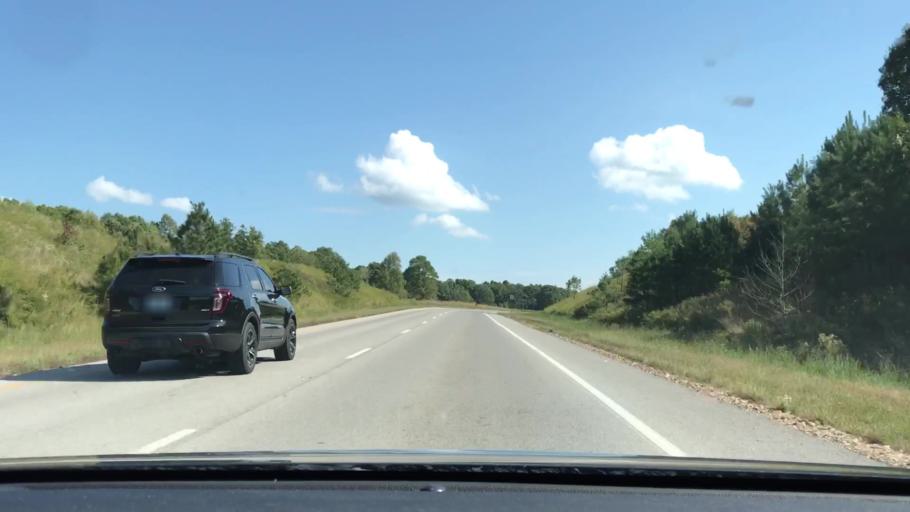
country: US
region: Kentucky
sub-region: Trigg County
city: Cadiz
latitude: 36.7776
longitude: -88.0814
